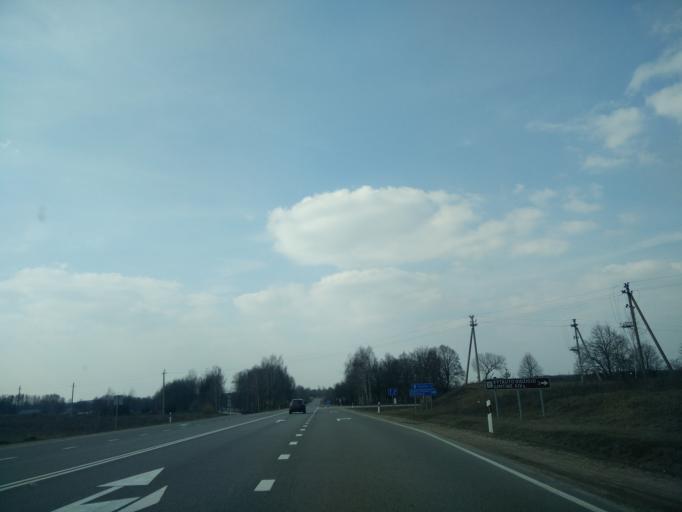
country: LT
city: Trakai
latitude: 54.6273
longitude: 24.9607
